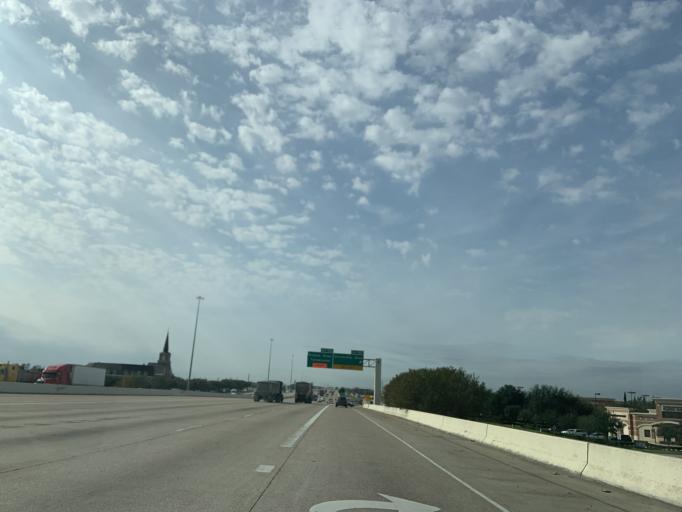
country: US
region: Texas
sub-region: Fort Bend County
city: Sugar Land
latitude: 29.5892
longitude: -95.6352
